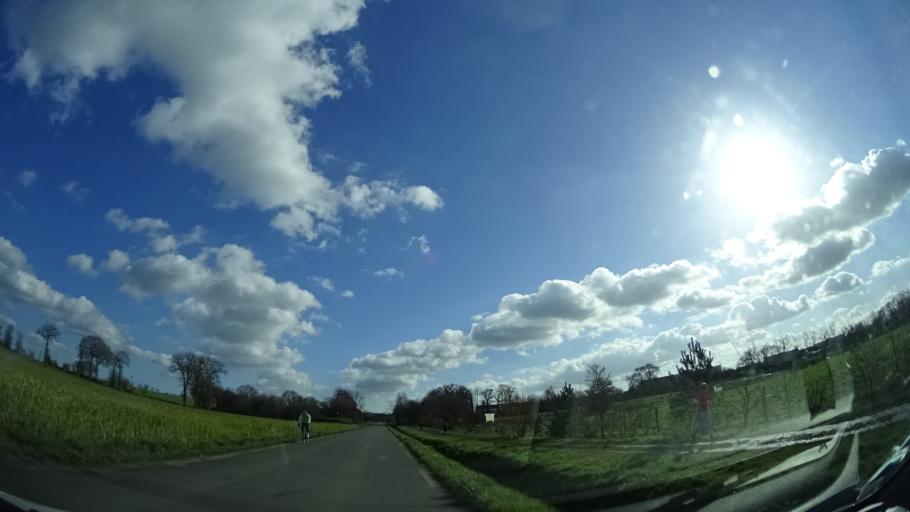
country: FR
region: Brittany
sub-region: Departement d'Ille-et-Vilaine
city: Pace
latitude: 48.1594
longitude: -1.7607
